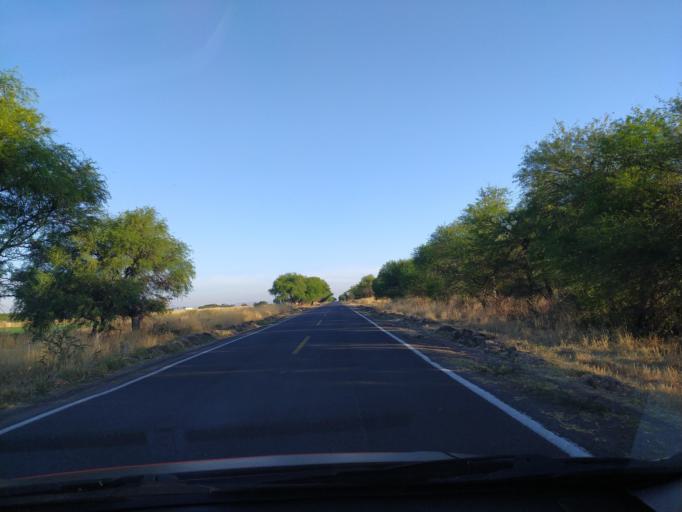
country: MX
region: Guanajuato
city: Ciudad Manuel Doblado
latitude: 20.7584
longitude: -101.8272
